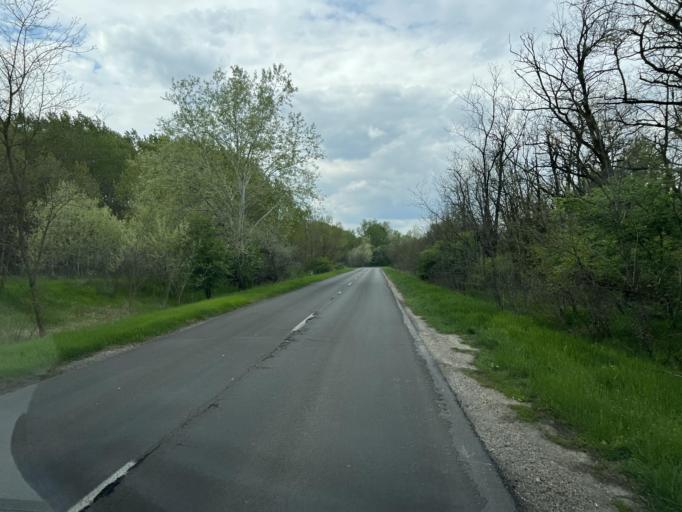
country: HU
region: Pest
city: Hernad
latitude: 47.1901
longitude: 19.4196
